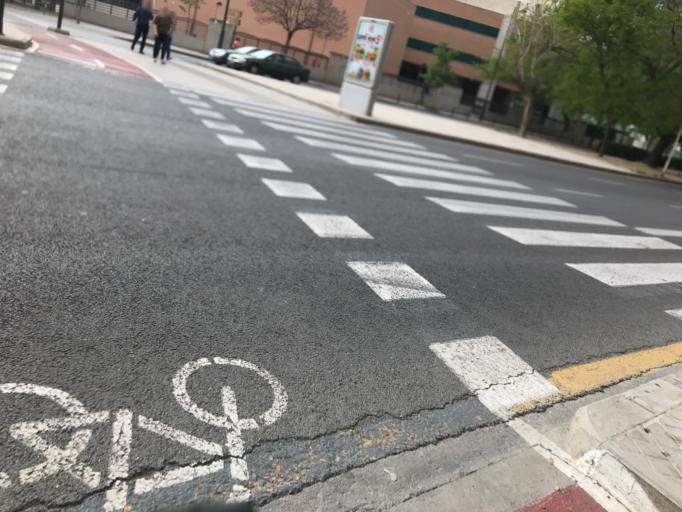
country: ES
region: Valencia
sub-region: Provincia de Valencia
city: Valencia
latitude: 39.4623
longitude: -0.3529
